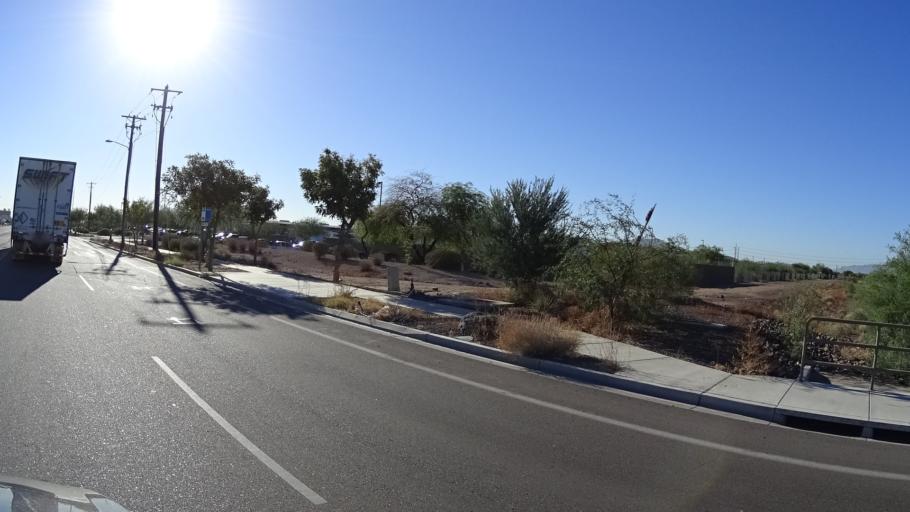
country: US
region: Arizona
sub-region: Maricopa County
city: Laveen
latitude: 33.4223
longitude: -112.1739
